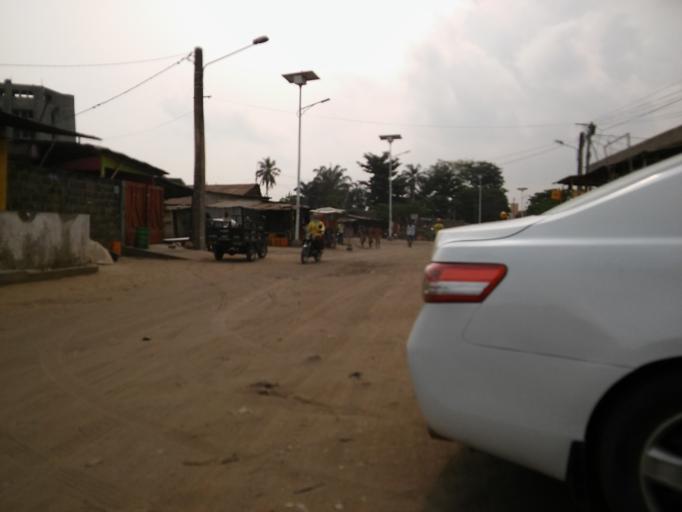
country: BJ
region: Littoral
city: Cotonou
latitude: 6.3908
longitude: 2.3842
